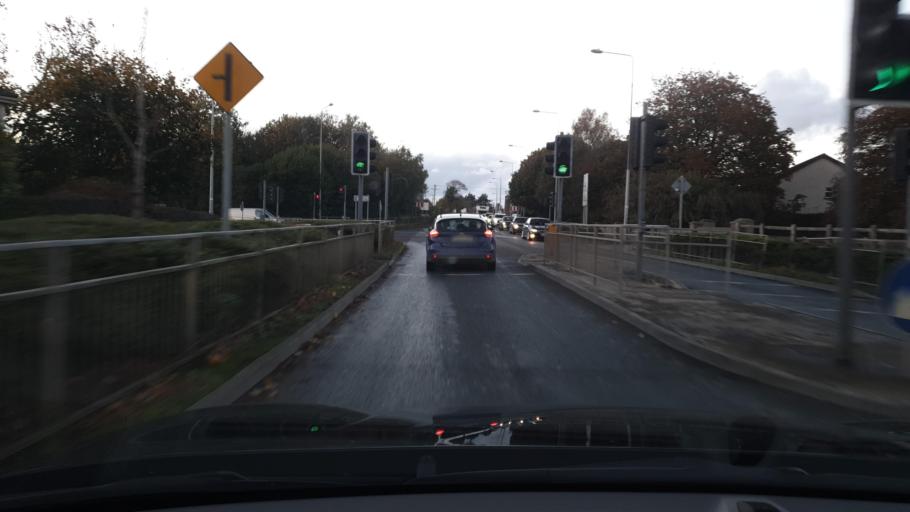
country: IE
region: Leinster
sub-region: Lu
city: Drogheda
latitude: 53.7244
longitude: -6.3640
